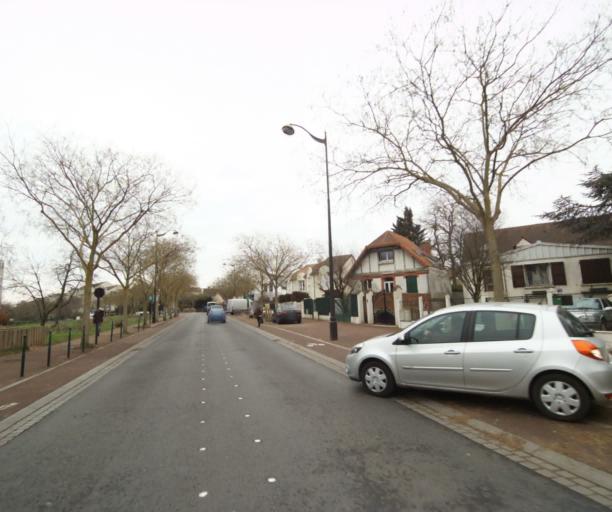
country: FR
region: Ile-de-France
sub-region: Departement des Hauts-de-Seine
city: Rueil-Malmaison
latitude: 48.8640
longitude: 2.1900
